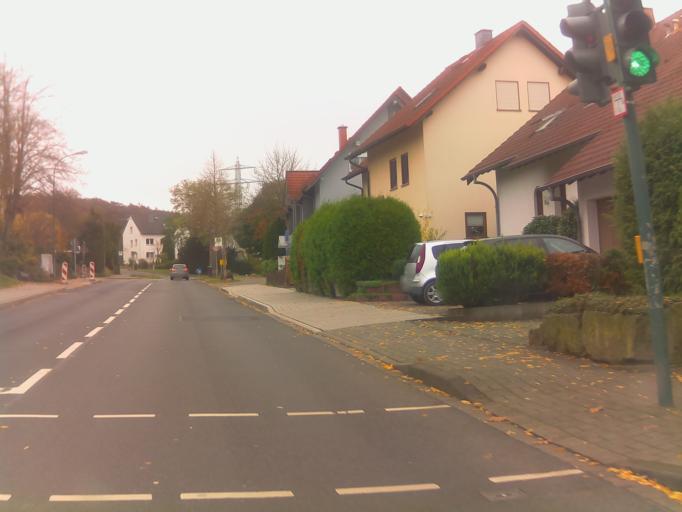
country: DE
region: Hesse
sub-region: Regierungsbezirk Kassel
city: Fulda
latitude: 50.5768
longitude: 9.6788
